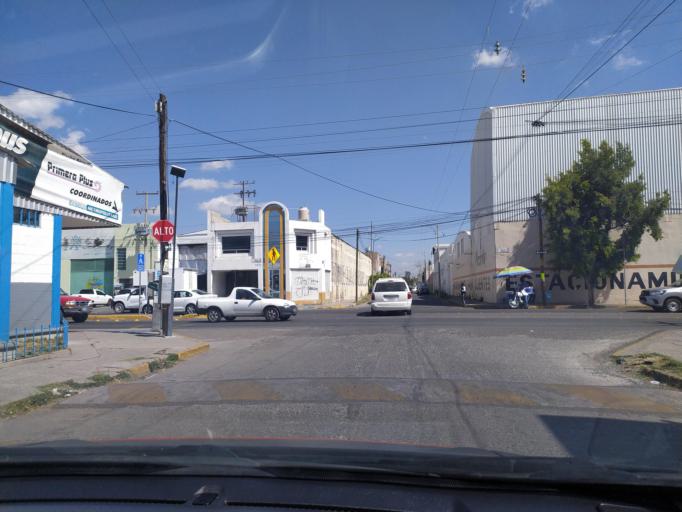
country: LA
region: Oudomxai
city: Muang La
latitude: 21.0247
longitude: 101.8520
